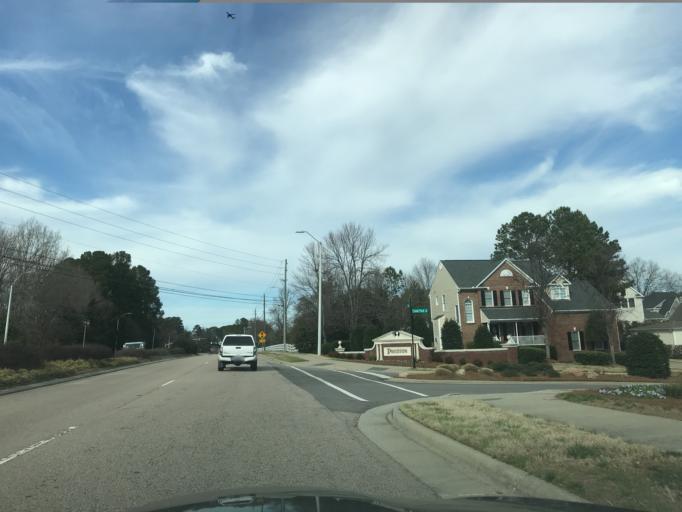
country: US
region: North Carolina
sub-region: Wake County
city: Morrisville
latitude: 35.8010
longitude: -78.8485
